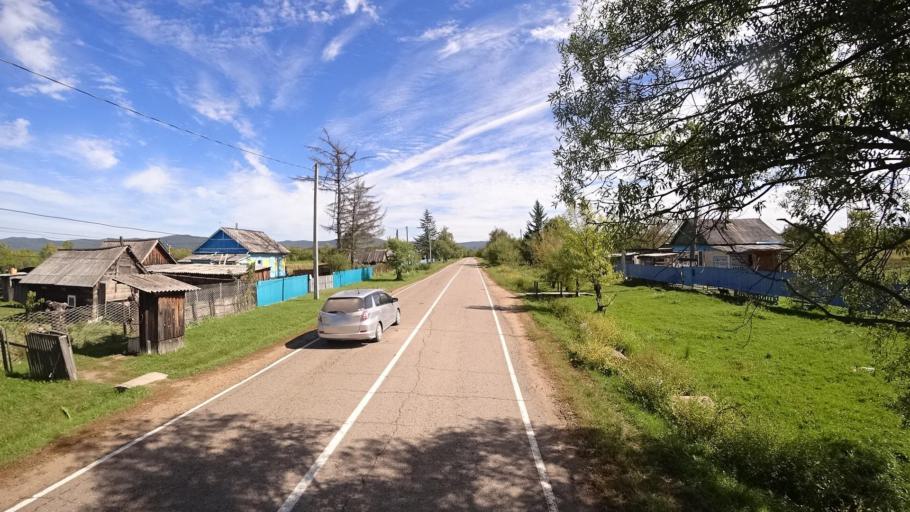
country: RU
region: Primorskiy
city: Yakovlevka
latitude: 44.4292
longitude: 133.5702
